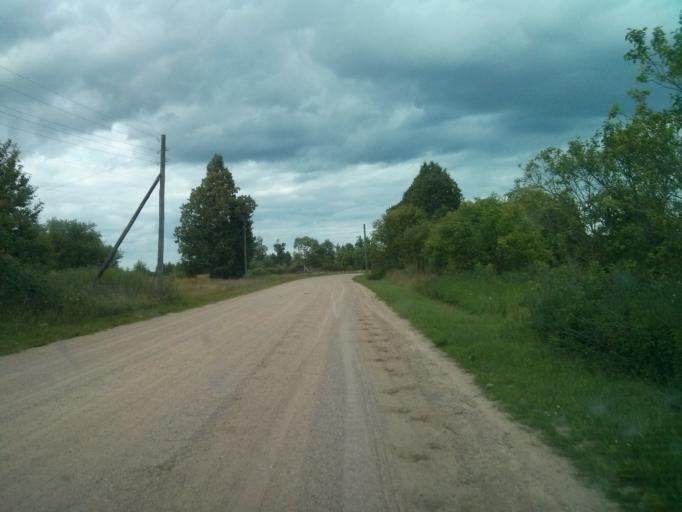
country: BY
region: Minsk
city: Plyeshchanitsy
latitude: 54.6039
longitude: 27.7893
